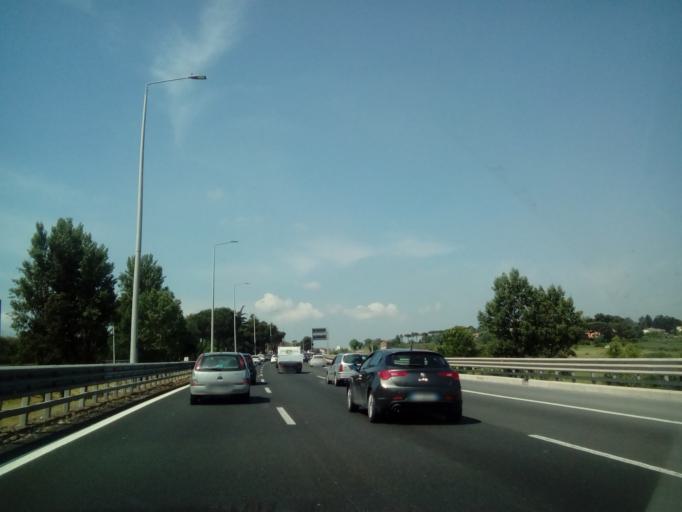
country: IT
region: Latium
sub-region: Citta metropolitana di Roma Capitale
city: Borgo Lotti
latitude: 41.8014
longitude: 12.5518
